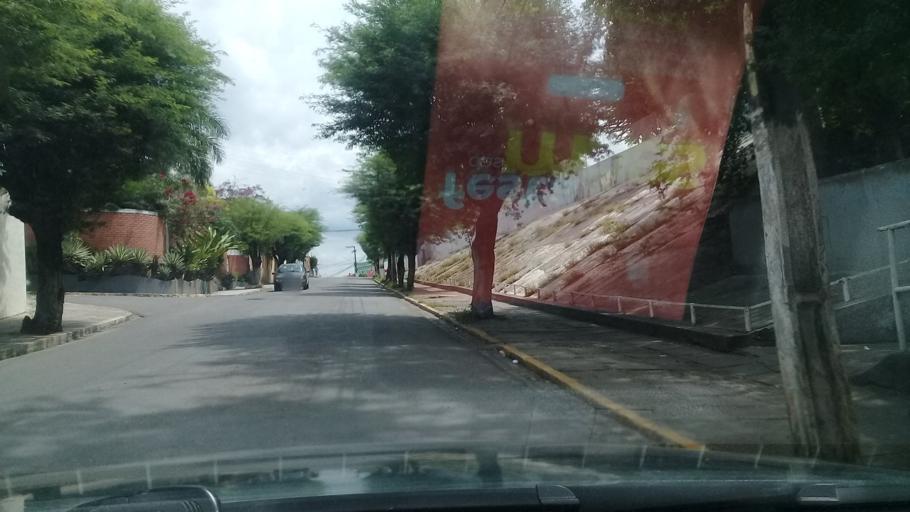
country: BR
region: Pernambuco
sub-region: Vitoria De Santo Antao
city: Vitoria de Santo Antao
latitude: -8.1138
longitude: -35.2874
